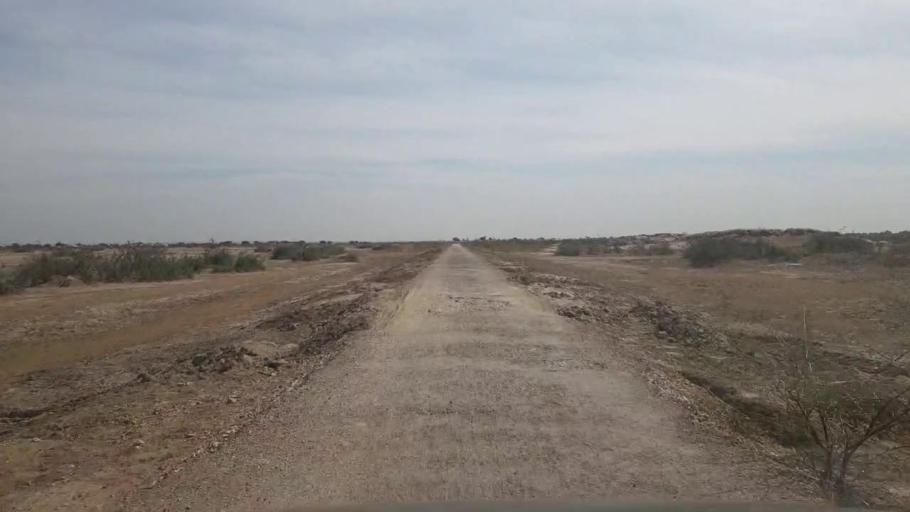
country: PK
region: Sindh
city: Kunri
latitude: 25.2173
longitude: 69.6217
